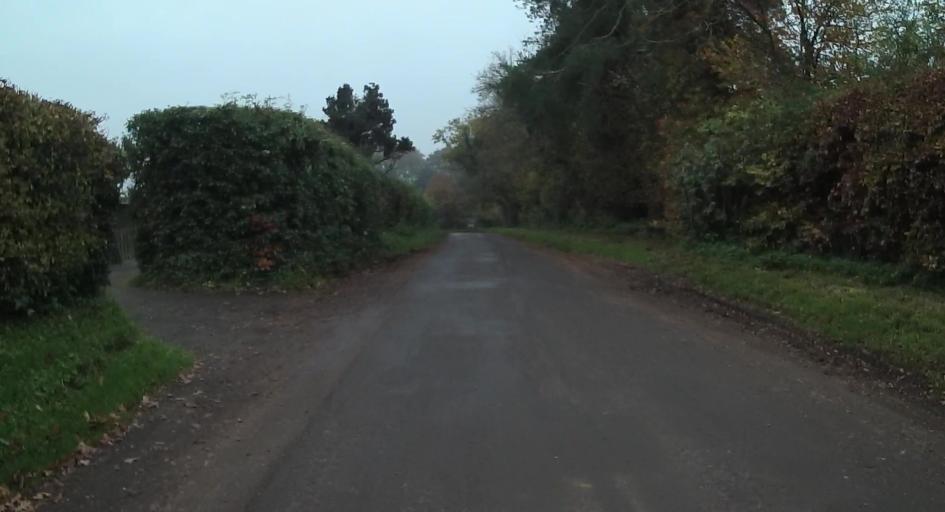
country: GB
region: England
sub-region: Hampshire
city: Old Basing
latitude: 51.2035
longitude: -1.0375
